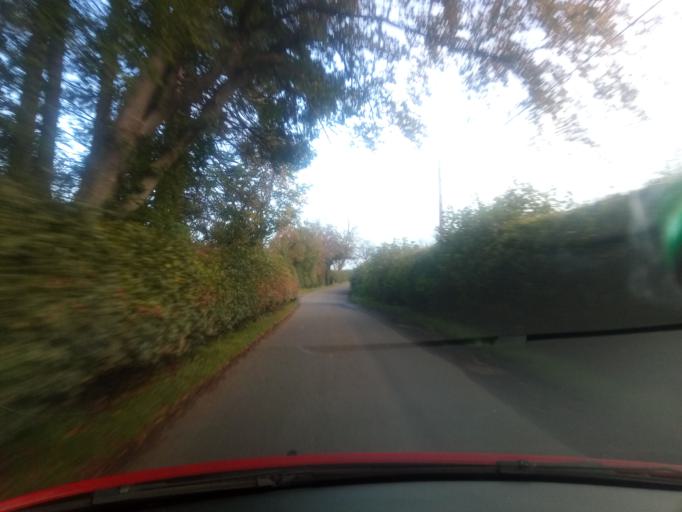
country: GB
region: Scotland
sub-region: The Scottish Borders
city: Jedburgh
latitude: 55.3781
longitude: -2.6473
